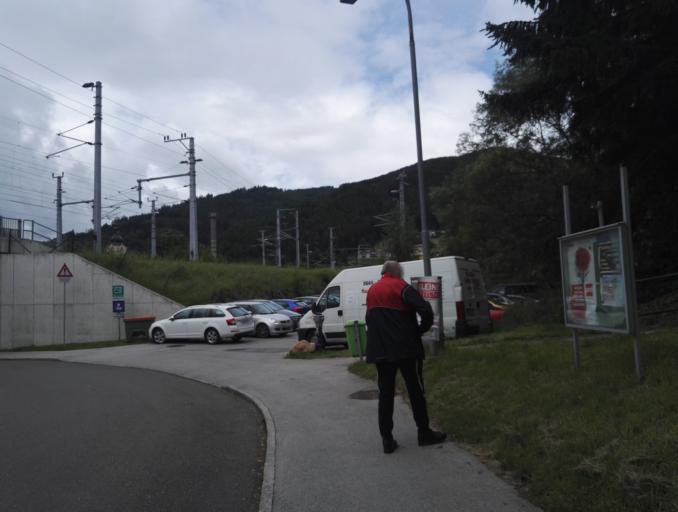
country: AT
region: Styria
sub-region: Politischer Bezirk Bruck-Muerzzuschlag
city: Muerzzuschlag
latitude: 47.6084
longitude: 15.6751
